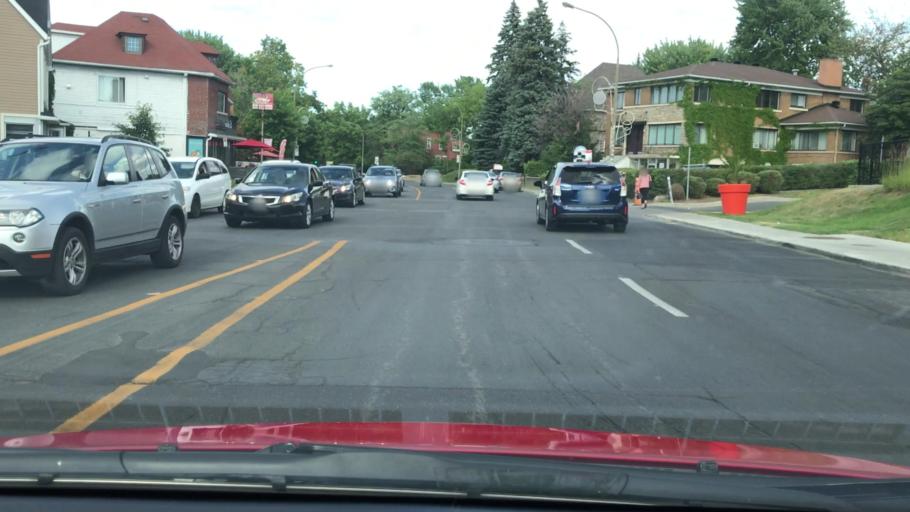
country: CA
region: Quebec
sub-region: Laval
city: Laval
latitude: 45.5323
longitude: -73.7200
